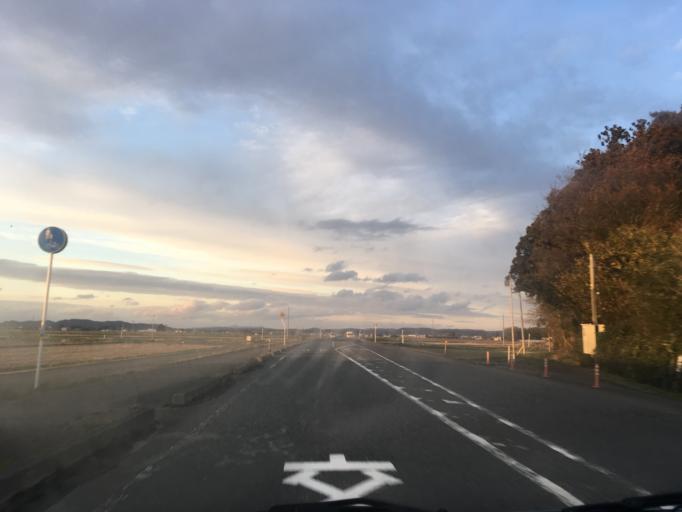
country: JP
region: Miyagi
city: Wakuya
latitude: 38.6946
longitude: 141.2604
